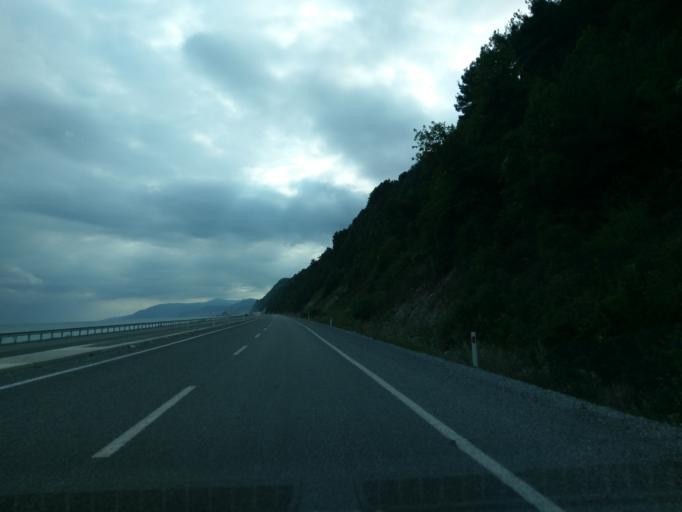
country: TR
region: Kastamonu
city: Catalzeytin
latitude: 41.9492
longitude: 34.2434
